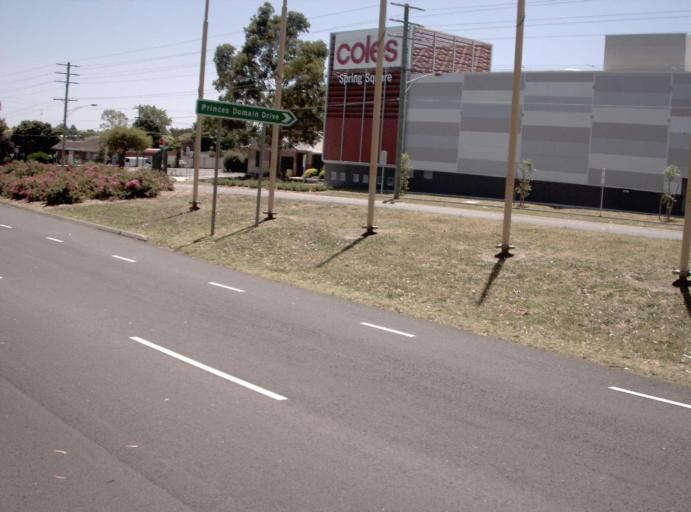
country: AU
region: Victoria
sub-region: Casey
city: Hallam
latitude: -38.0055
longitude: 145.2666
